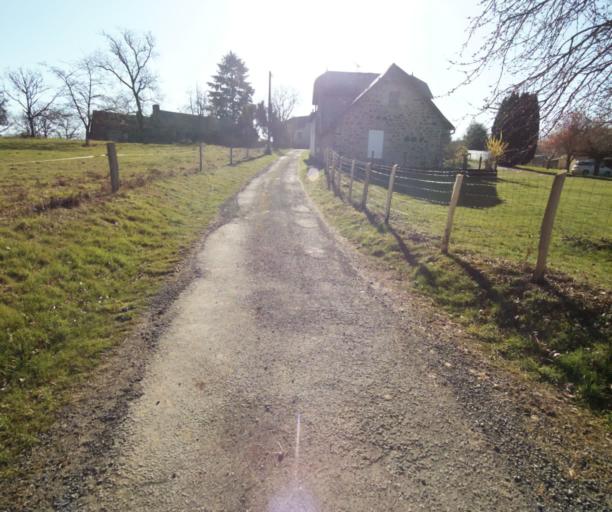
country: FR
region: Limousin
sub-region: Departement de la Correze
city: Saint-Clement
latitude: 45.3725
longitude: 1.6528
